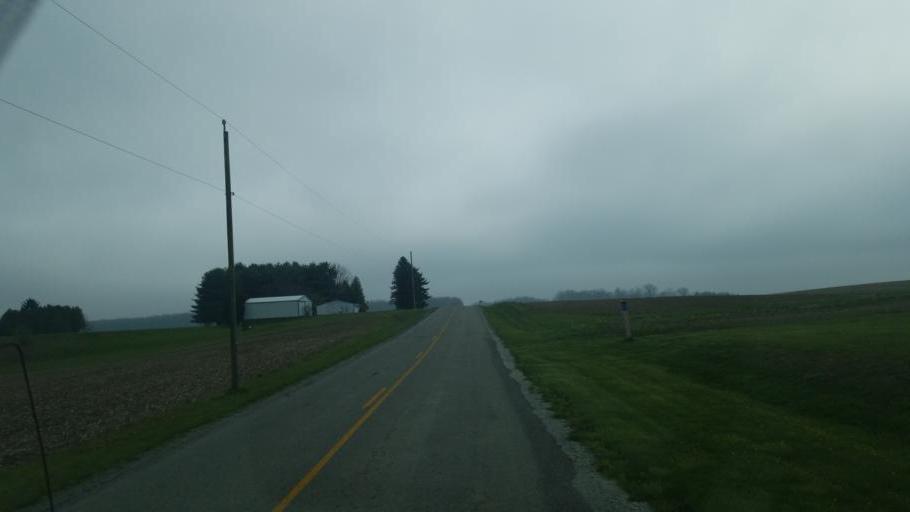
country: US
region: Ohio
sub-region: Hardin County
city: Kenton
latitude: 40.5549
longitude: -83.6411
